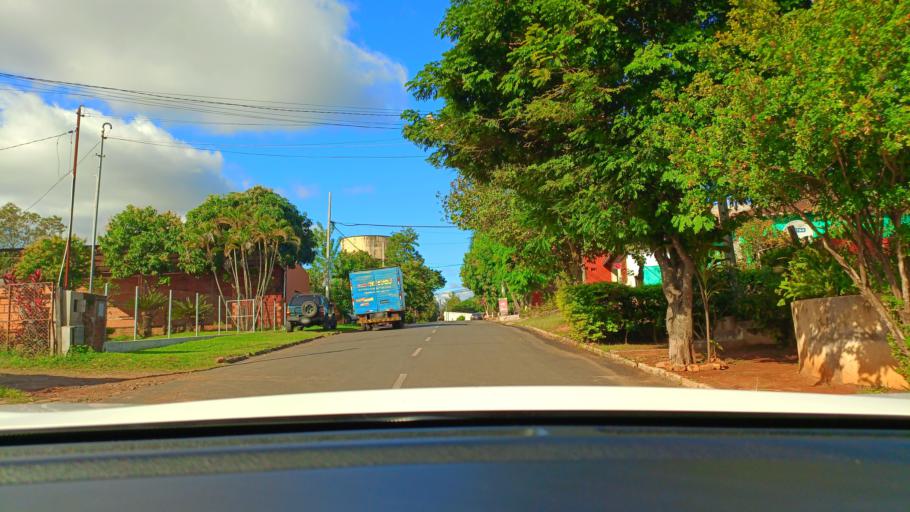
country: PY
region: San Pedro
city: Guayaybi
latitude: -24.6728
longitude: -56.4434
